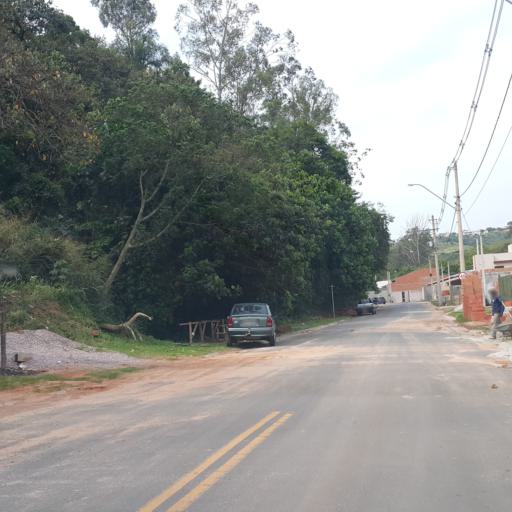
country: BR
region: Sao Paulo
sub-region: Louveira
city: Louveira
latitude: -23.0752
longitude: -46.9489
